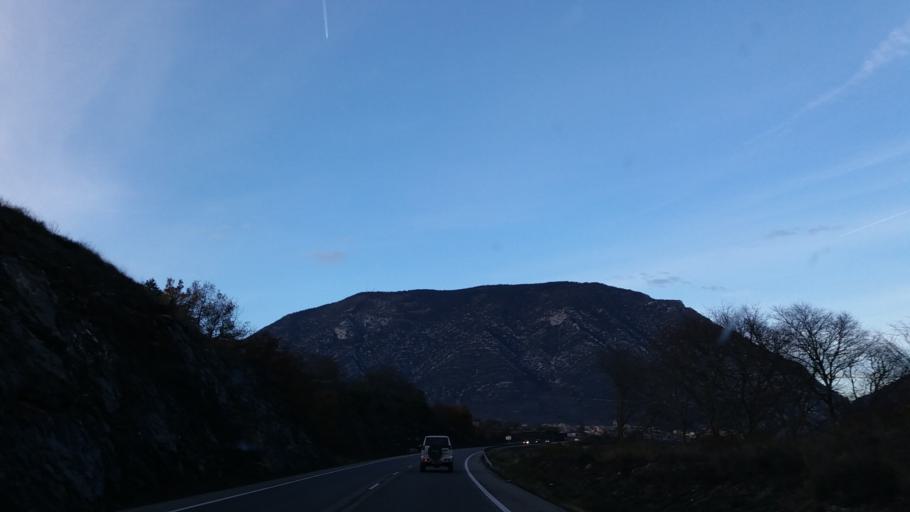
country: ES
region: Catalonia
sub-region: Provincia de Lleida
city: Coll de Nargo
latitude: 42.1985
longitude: 1.3275
